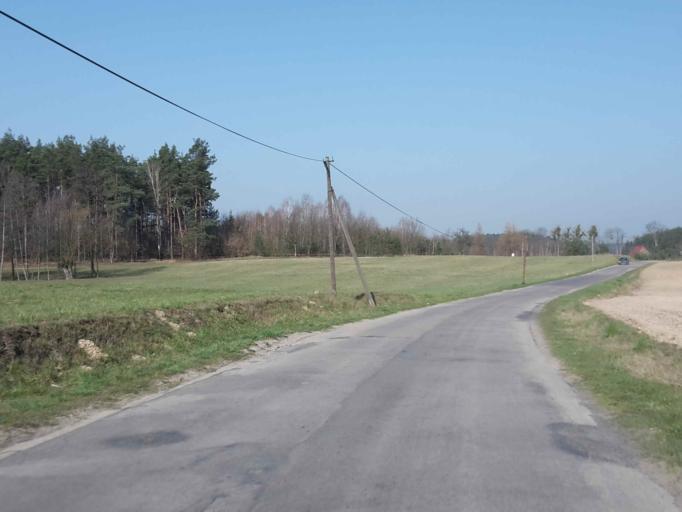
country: PL
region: Kujawsko-Pomorskie
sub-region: Powiat brodnicki
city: Brodnica
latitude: 53.3353
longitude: 19.3585
